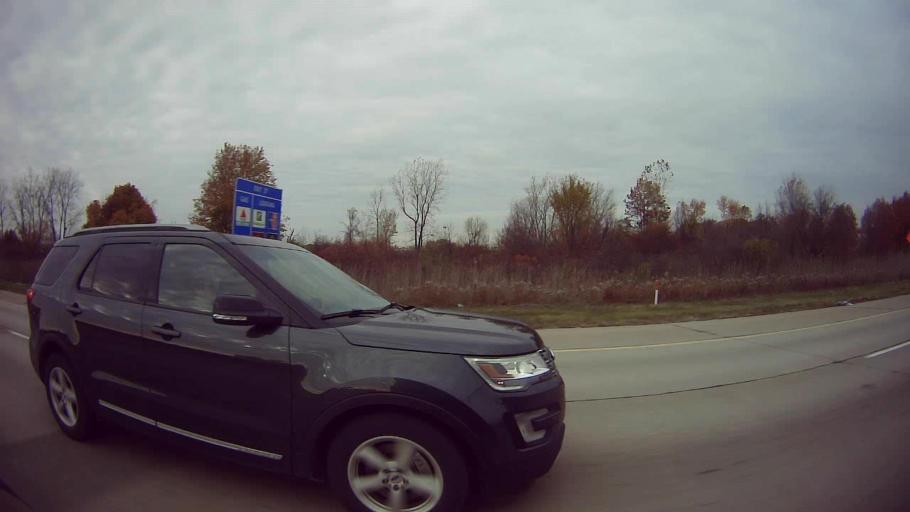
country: US
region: Michigan
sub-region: Wayne County
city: Southgate
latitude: 42.2190
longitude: -83.2153
